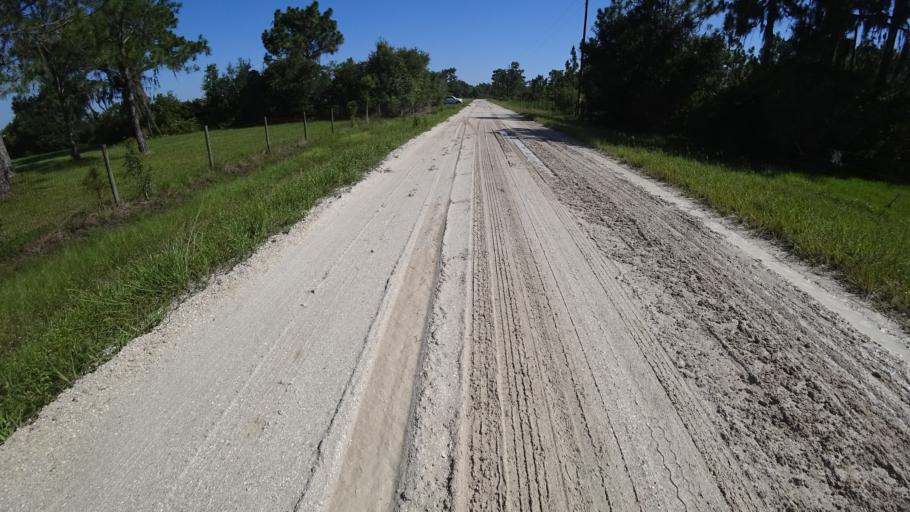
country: US
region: Florida
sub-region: Sarasota County
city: The Meadows
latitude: 27.4140
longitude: -82.2874
